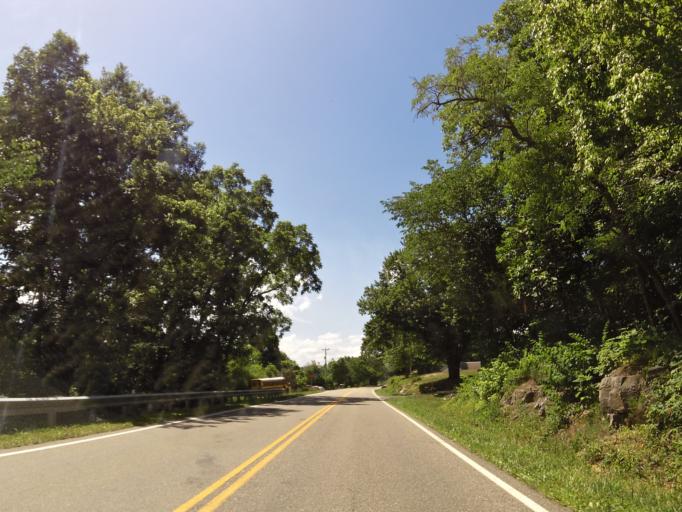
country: US
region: Virginia
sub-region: Lee County
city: Pennington Gap
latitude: 36.7147
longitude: -82.9735
